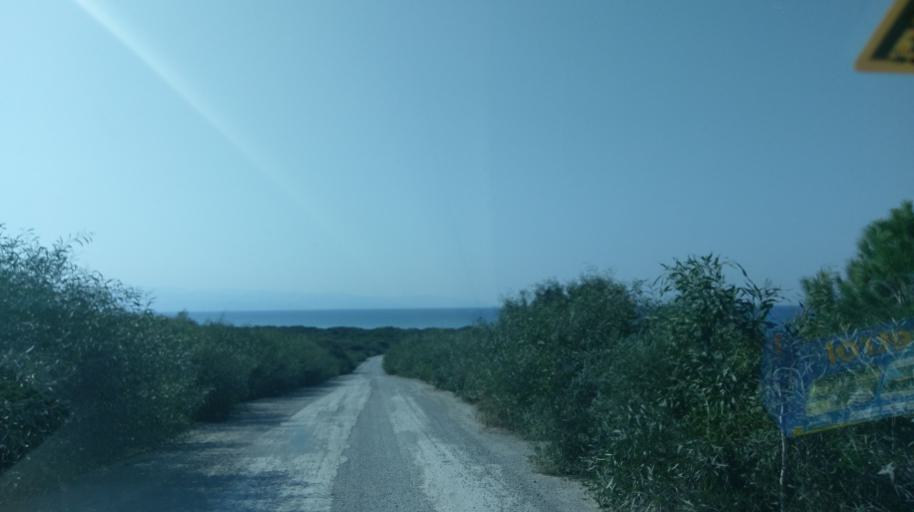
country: CY
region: Lefkosia
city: Morfou
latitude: 35.2826
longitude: 32.9433
